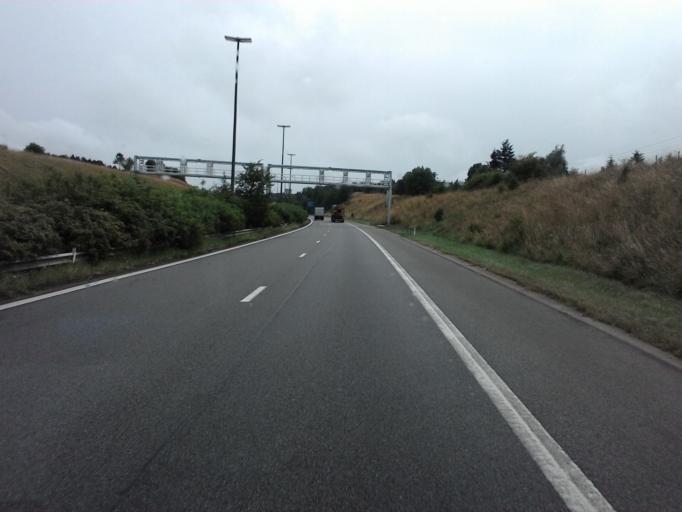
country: BE
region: Wallonia
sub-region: Province de Liege
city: Aywaille
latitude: 50.4374
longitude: 5.6986
